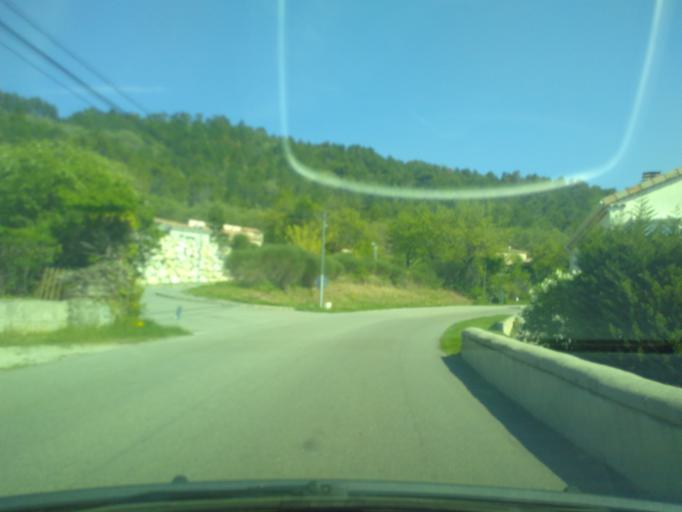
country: FR
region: Rhone-Alpes
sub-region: Departement de la Drome
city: La Begude-de-Mazenc
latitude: 44.6278
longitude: 4.9768
